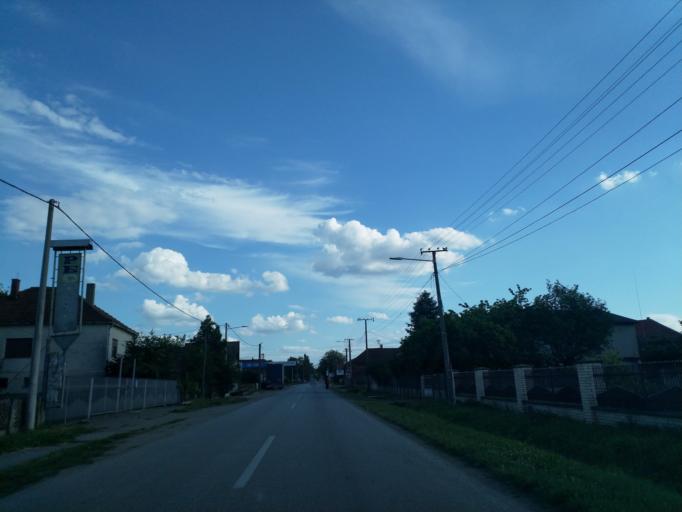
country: RS
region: Central Serbia
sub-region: Sumadijski Okrug
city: Lapovo
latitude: 44.1801
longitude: 21.0914
